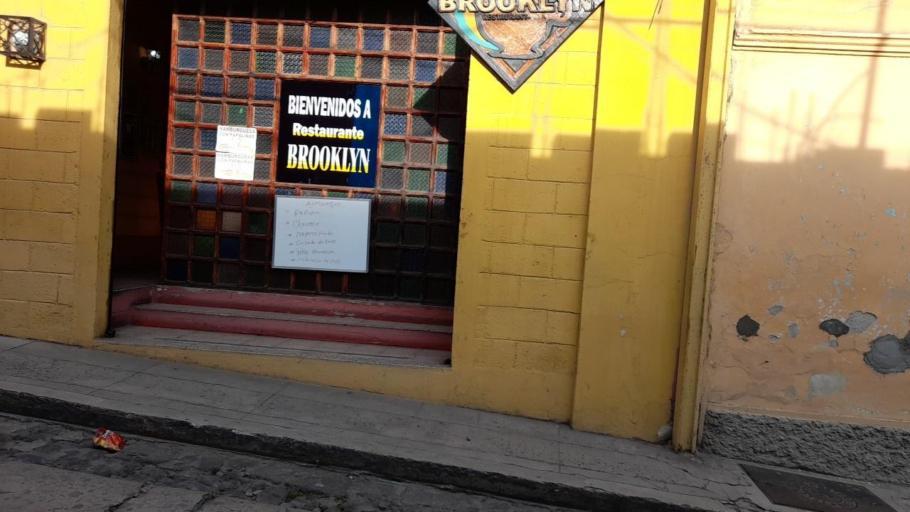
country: GT
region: Quetzaltenango
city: Quetzaltenango
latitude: 14.8383
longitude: -91.5200
